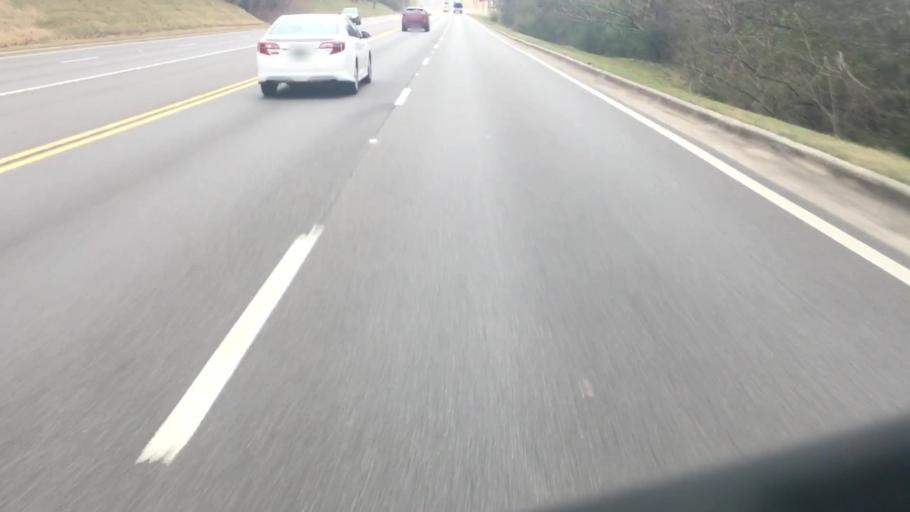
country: US
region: Alabama
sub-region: Jefferson County
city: Hoover
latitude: 33.3572
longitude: -86.8363
